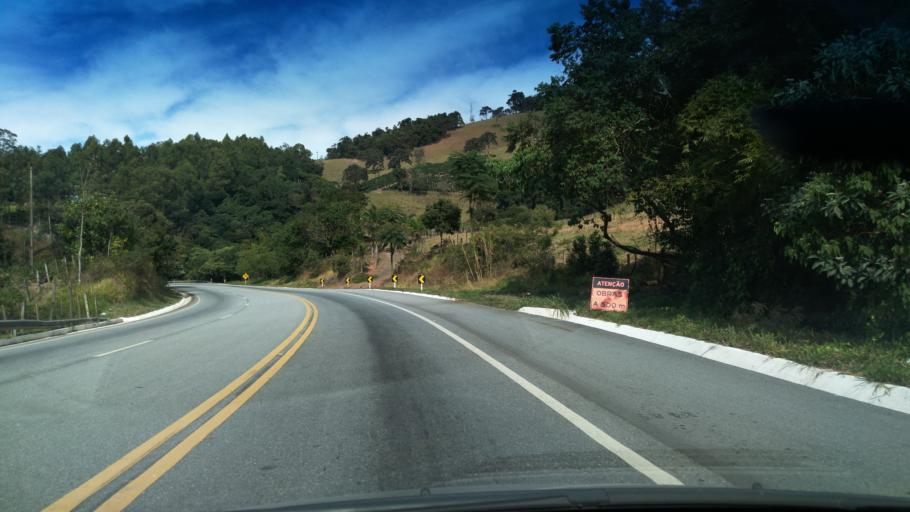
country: BR
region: Minas Gerais
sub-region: Borda Da Mata
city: Borda da Mata
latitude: -22.1325
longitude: -46.1496
